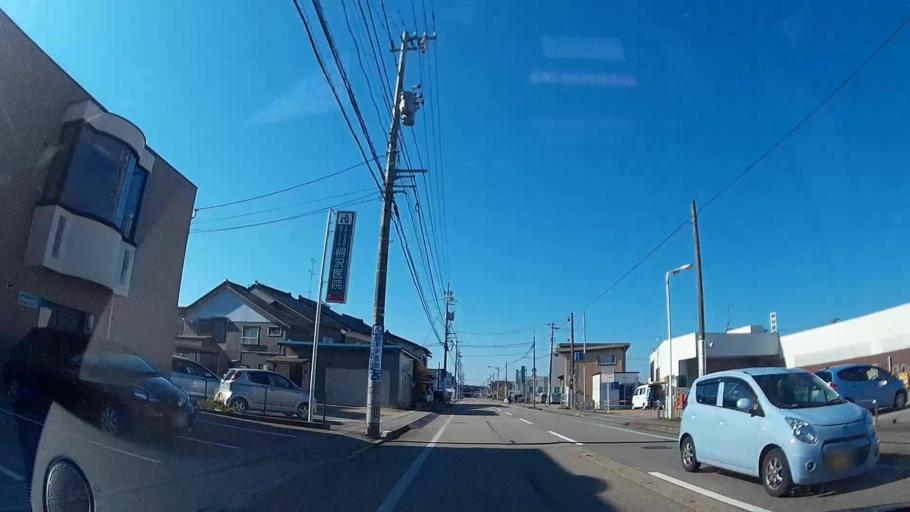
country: JP
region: Toyama
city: Nanto-shi
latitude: 36.6382
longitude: 136.9486
